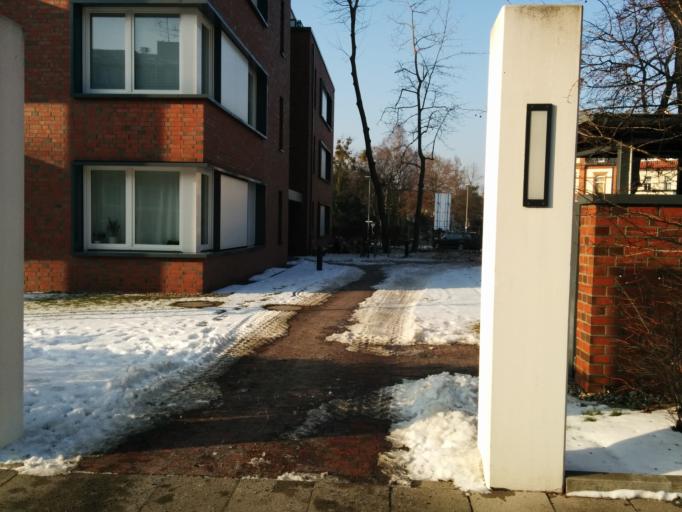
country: DE
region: Lower Saxony
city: Hannover
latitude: 52.3911
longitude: 9.7102
